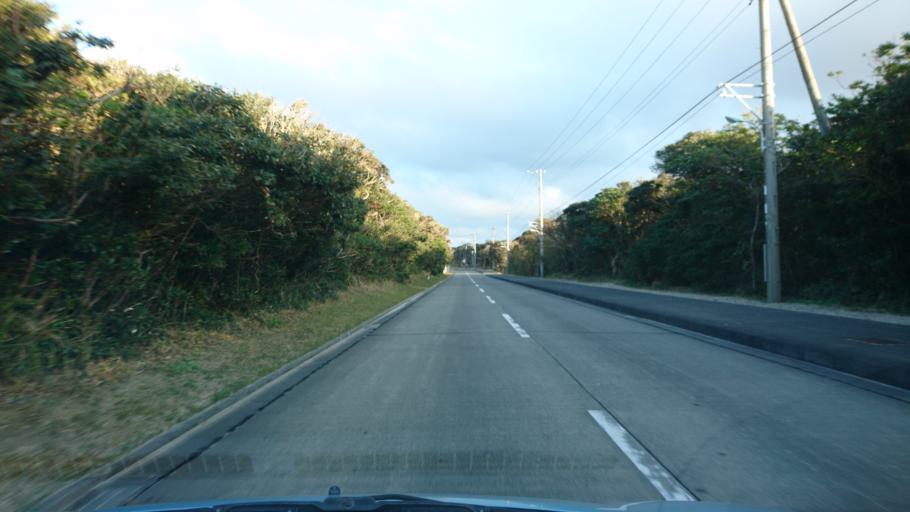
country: JP
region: Shizuoka
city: Shimoda
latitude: 34.3633
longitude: 139.2531
